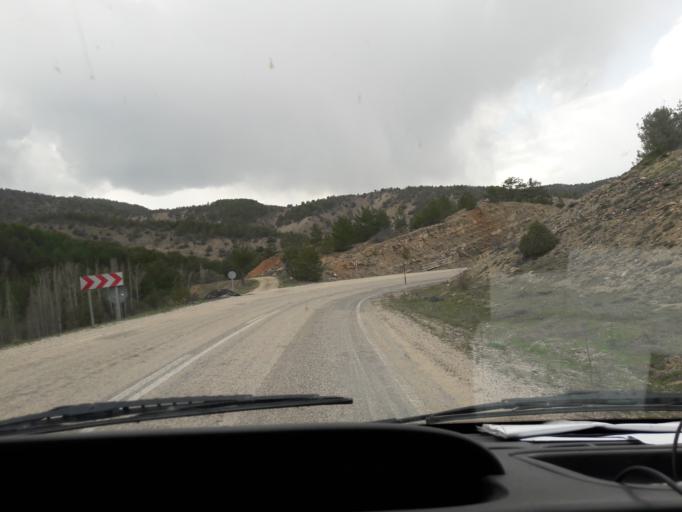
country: TR
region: Giresun
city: Alucra
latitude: 40.2768
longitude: 38.8232
